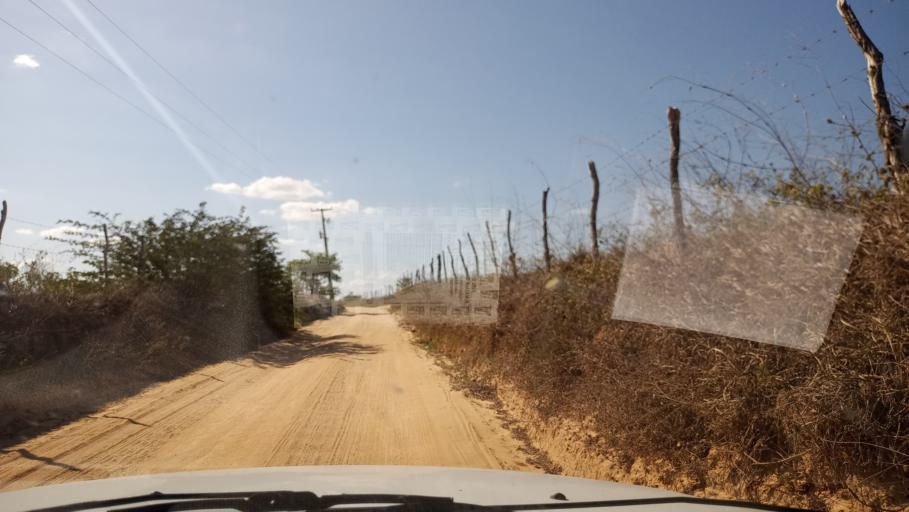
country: BR
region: Rio Grande do Norte
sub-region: Brejinho
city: Brejinho
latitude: -6.1788
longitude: -35.4538
